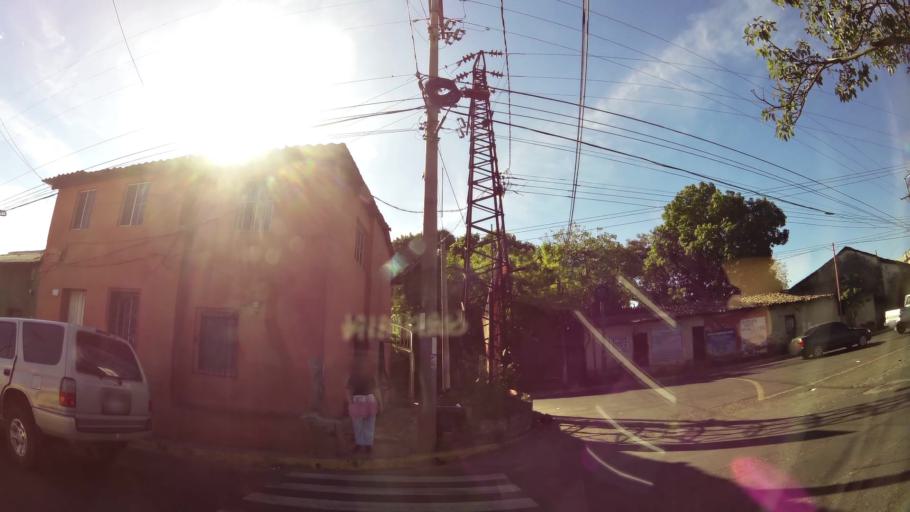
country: SV
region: Santa Ana
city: Santa Ana
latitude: 13.9825
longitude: -89.5749
